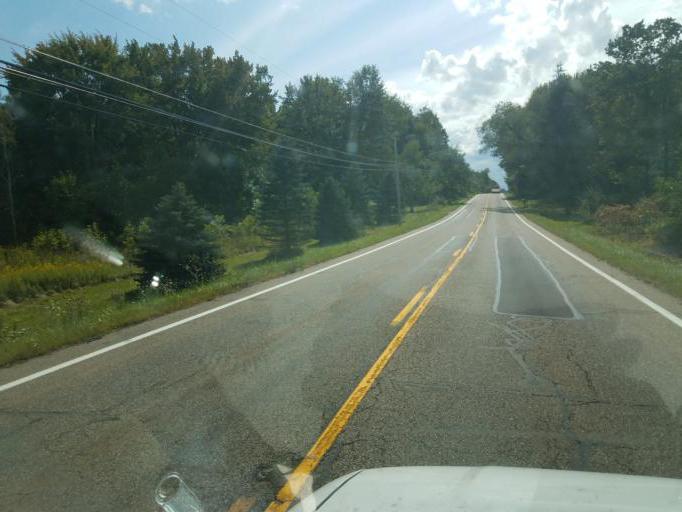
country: US
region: Ohio
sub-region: Portage County
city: Mantua
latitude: 41.2202
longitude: -81.1660
